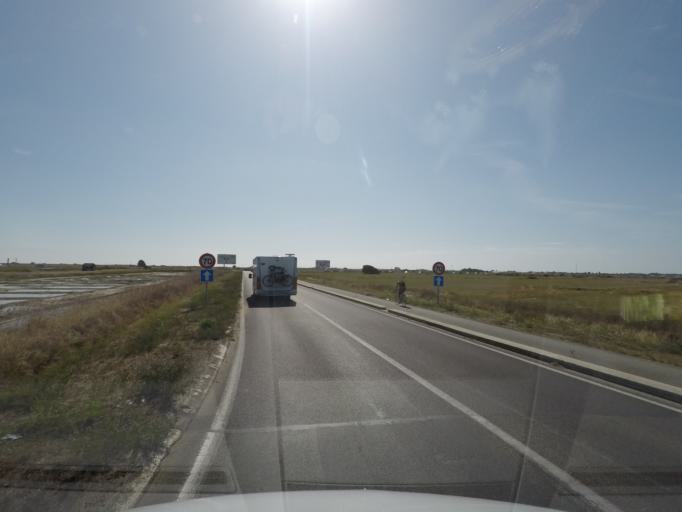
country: FR
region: Pays de la Loire
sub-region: Departement de la Vendee
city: La Gueriniere
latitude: 46.9905
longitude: -2.2509
